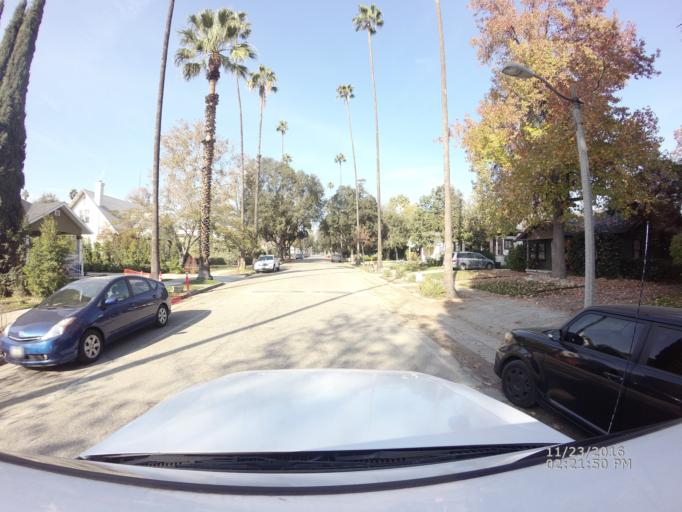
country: US
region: California
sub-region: Los Angeles County
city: South Pasadena
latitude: 34.1023
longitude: -118.1425
